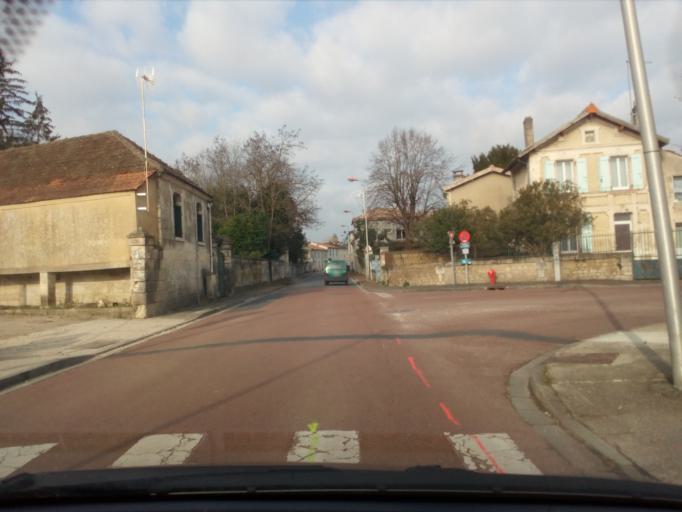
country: FR
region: Poitou-Charentes
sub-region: Departement de la Charente
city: Gond-Pontouvre
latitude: 45.6662
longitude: 0.1615
